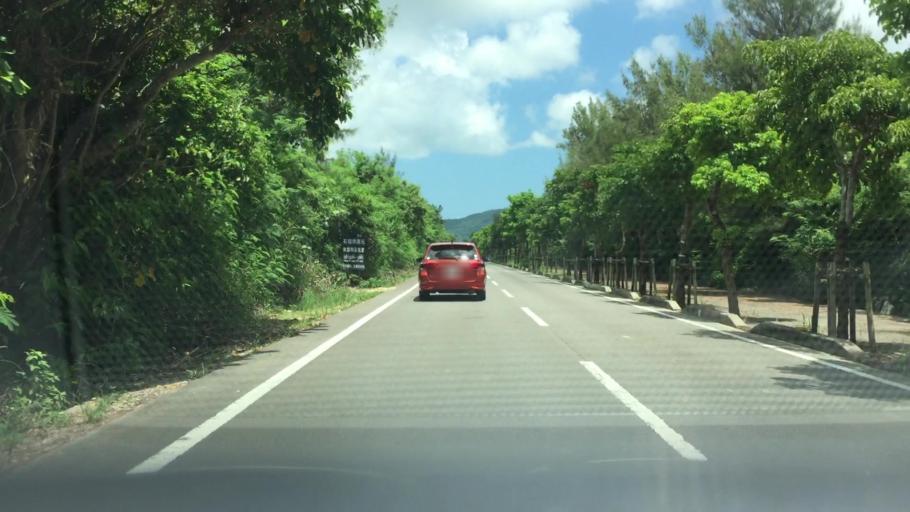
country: JP
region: Okinawa
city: Ishigaki
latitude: 24.3959
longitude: 124.1414
